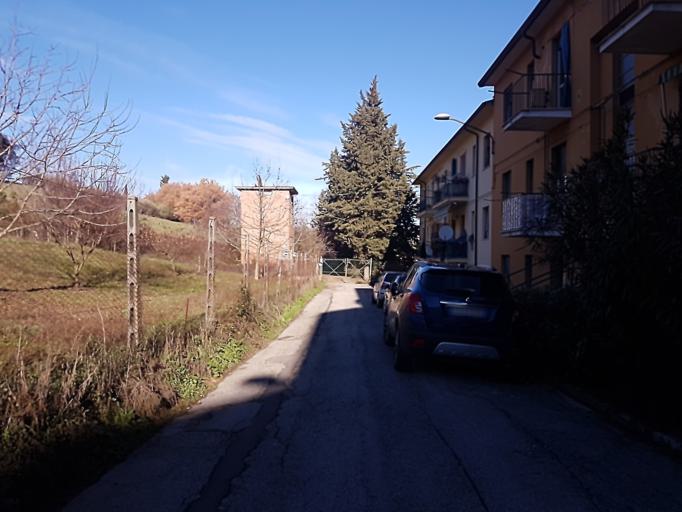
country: IT
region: Umbria
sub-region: Provincia di Perugia
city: Perugia
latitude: 43.0968
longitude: 12.3813
